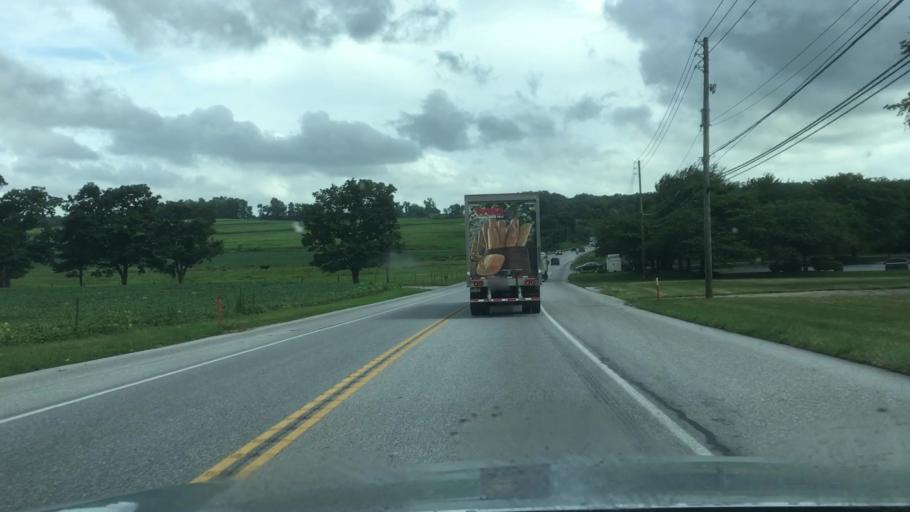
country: US
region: Pennsylvania
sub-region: Lancaster County
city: Gap
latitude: 39.9742
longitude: -76.0083
